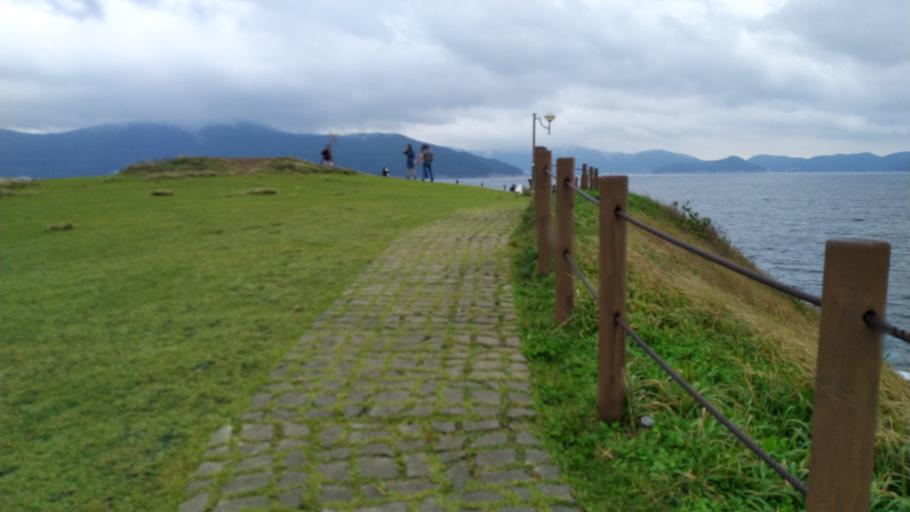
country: KR
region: Gyeongsangnam-do
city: Kyosai
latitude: 34.7443
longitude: 128.6632
